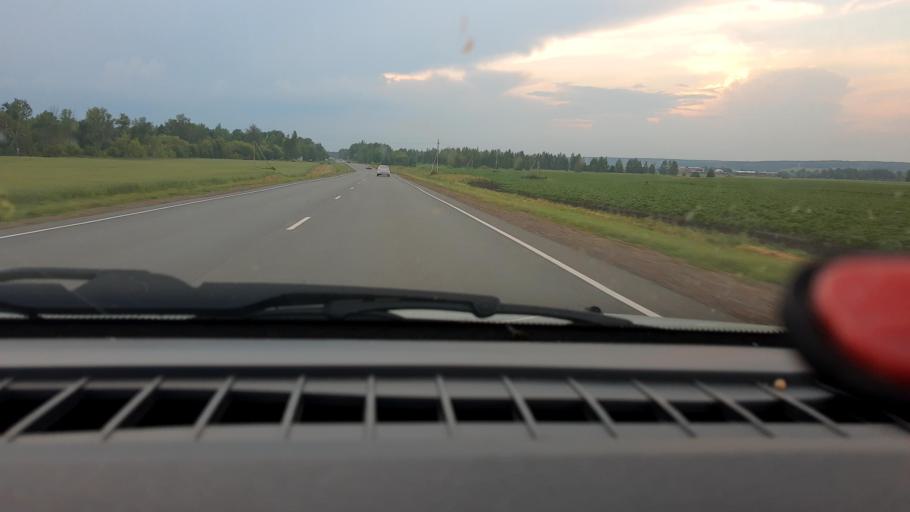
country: RU
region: Nizjnij Novgorod
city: Arzamas
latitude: 55.2805
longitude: 43.9552
